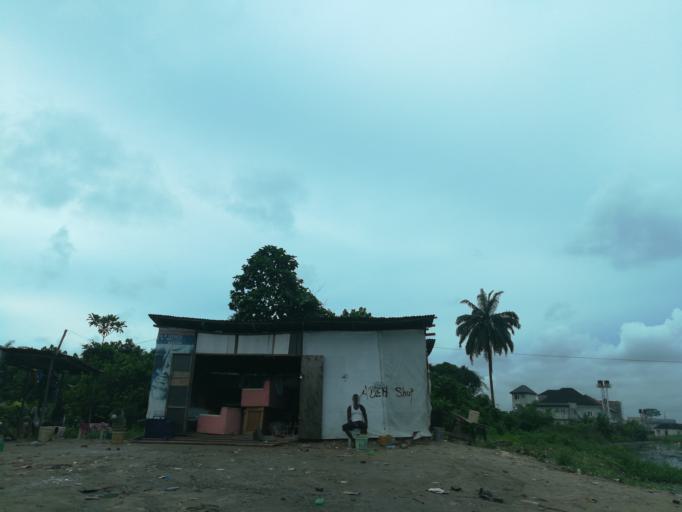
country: NG
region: Rivers
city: Port Harcourt
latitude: 4.8195
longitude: 6.9882
